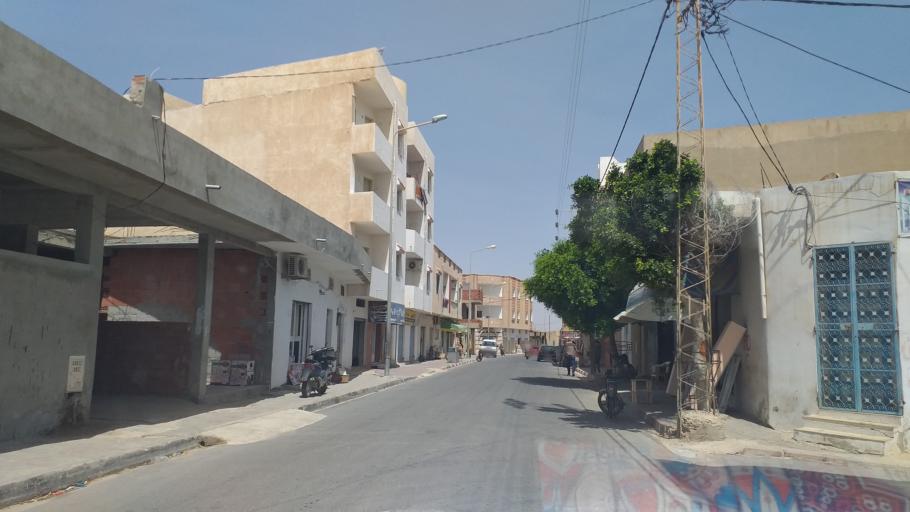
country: TN
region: Qabis
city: Gabes
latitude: 33.9416
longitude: 10.0641
